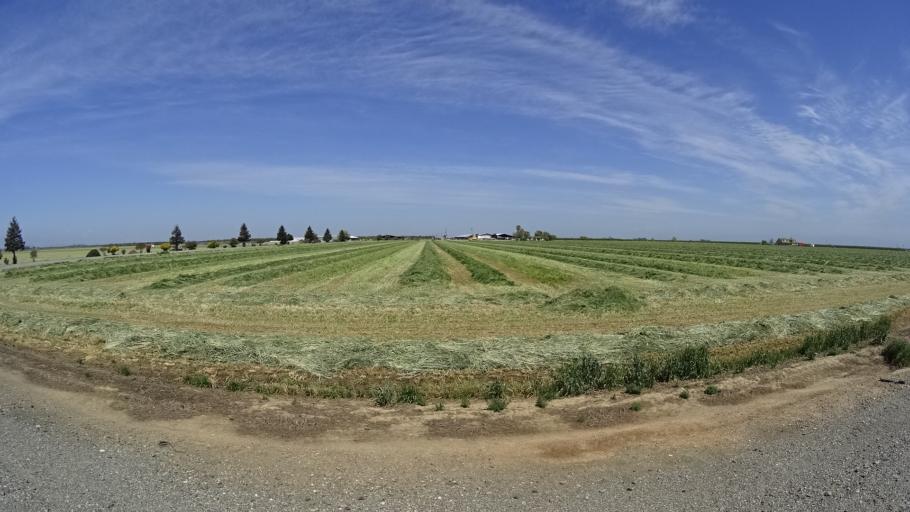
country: US
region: California
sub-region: Glenn County
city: Orland
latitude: 39.6527
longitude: -122.1502
